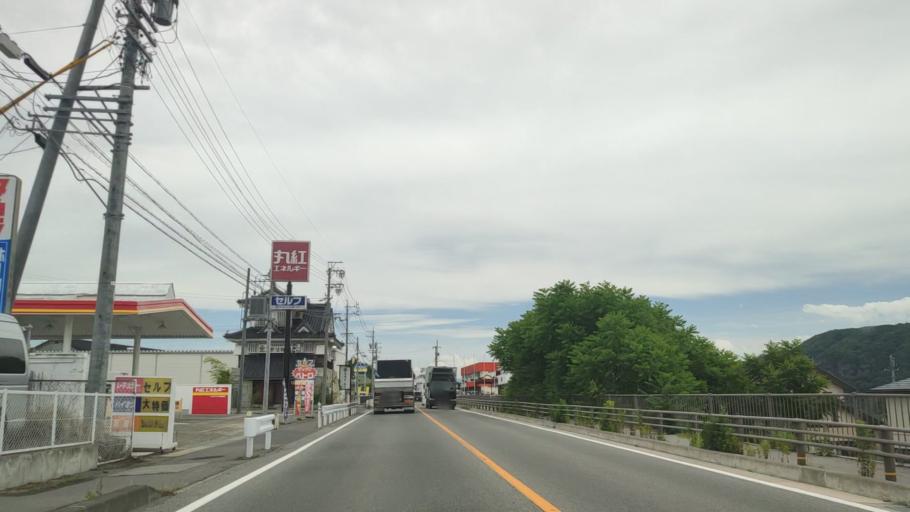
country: JP
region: Nagano
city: Komoro
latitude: 36.3478
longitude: 138.3678
